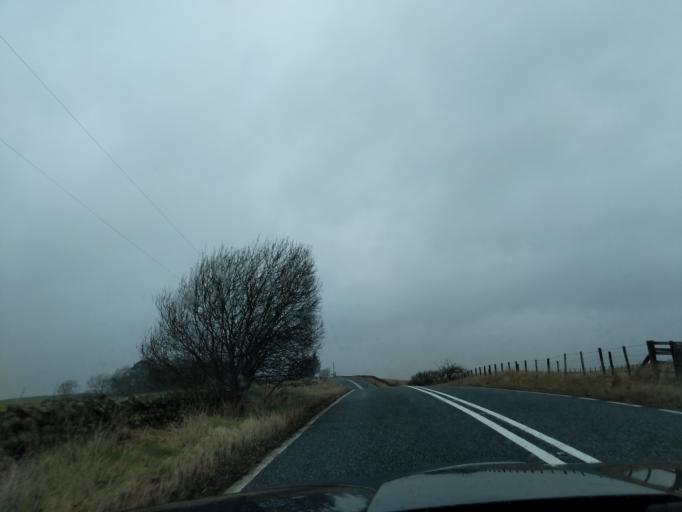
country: GB
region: England
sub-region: Northumberland
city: Rochester
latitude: 55.2483
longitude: -2.2184
